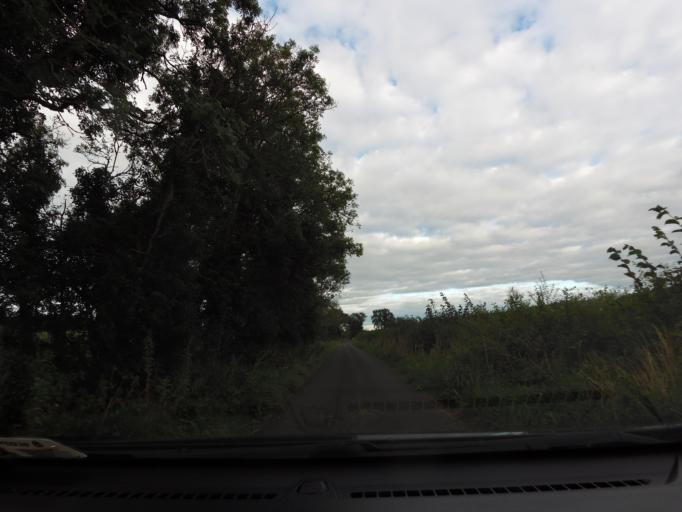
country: IE
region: Connaught
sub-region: County Galway
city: Loughrea
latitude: 53.1488
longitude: -8.5124
